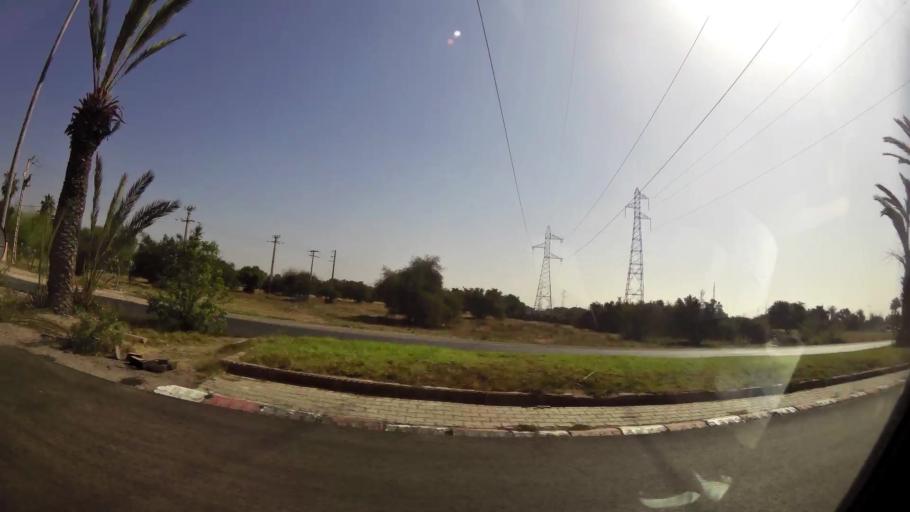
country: MA
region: Souss-Massa-Draa
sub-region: Inezgane-Ait Mellou
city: Inezgane
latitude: 30.3560
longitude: -9.4849
